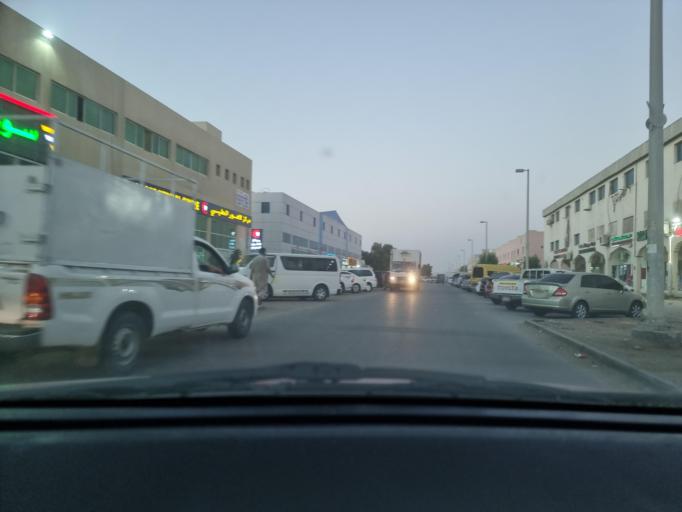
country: AE
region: Abu Dhabi
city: Abu Dhabi
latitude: 24.3489
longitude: 54.5190
